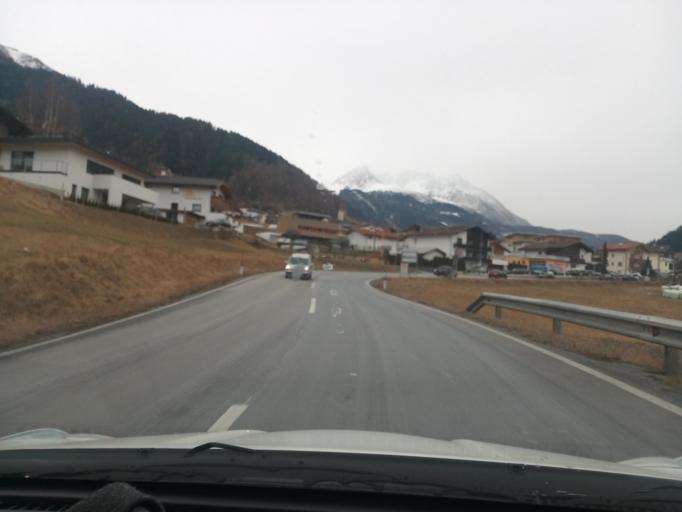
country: AT
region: Tyrol
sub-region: Politischer Bezirk Landeck
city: Nauders
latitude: 46.8973
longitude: 10.4983
